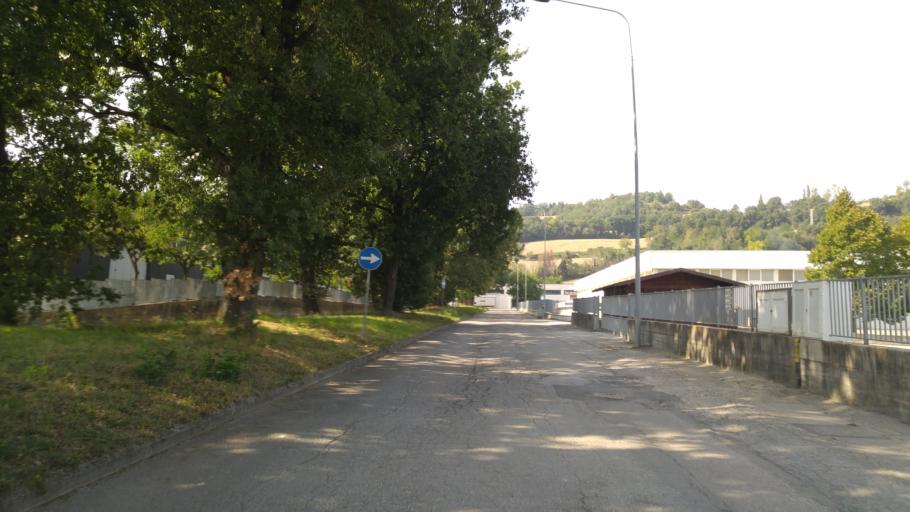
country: IT
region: The Marches
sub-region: Provincia di Pesaro e Urbino
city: Fermignano
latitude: 43.6932
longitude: 12.6522
